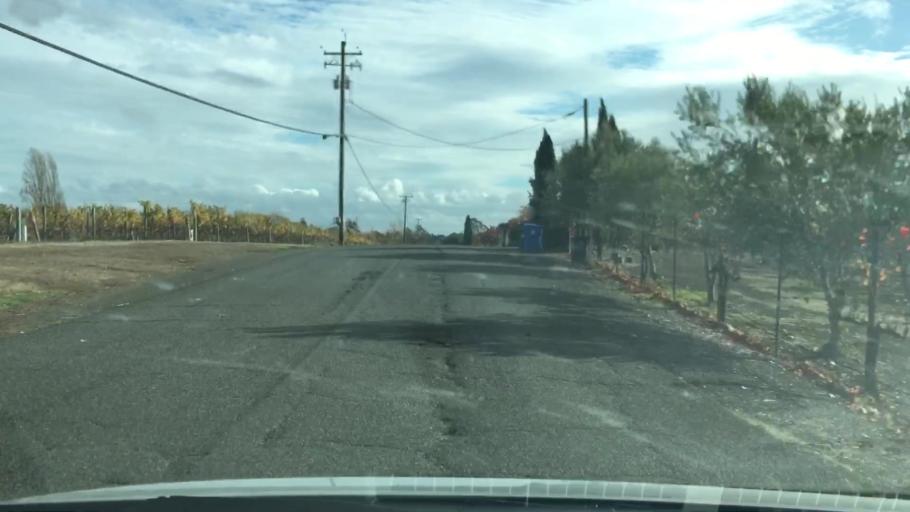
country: US
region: California
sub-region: Napa County
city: Napa
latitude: 38.2658
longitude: -122.3449
